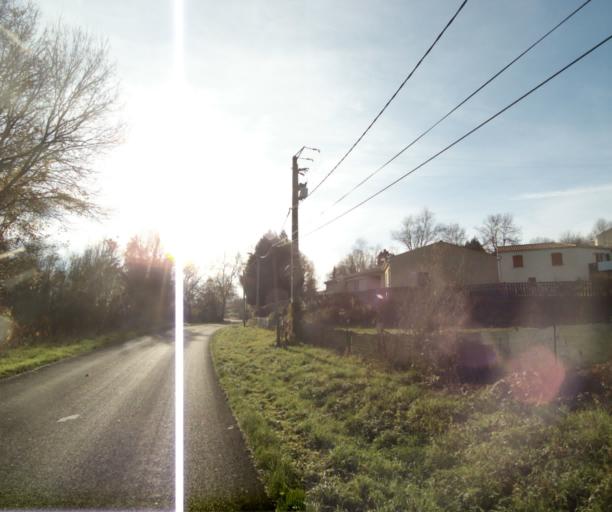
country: FR
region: Poitou-Charentes
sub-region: Departement de la Charente-Maritime
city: Chaniers
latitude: 45.7236
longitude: -0.5202
